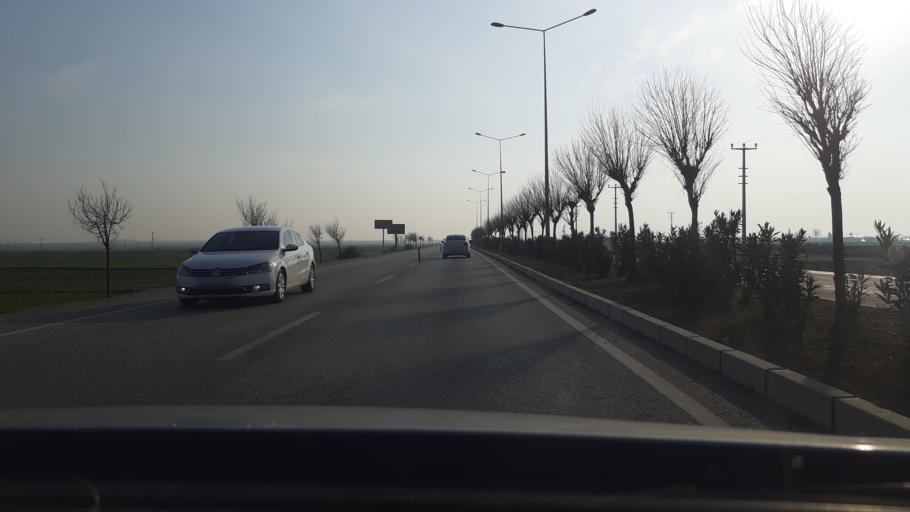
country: TR
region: Hatay
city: Serinyol
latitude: 36.3712
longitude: 36.2461
